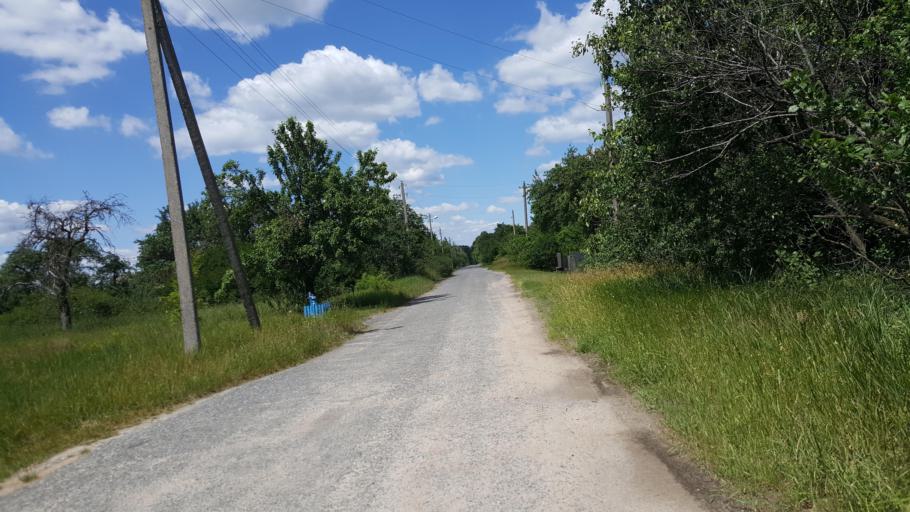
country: PL
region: Podlasie
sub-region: Powiat hajnowski
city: Czeremcha
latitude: 52.5081
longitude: 23.5481
